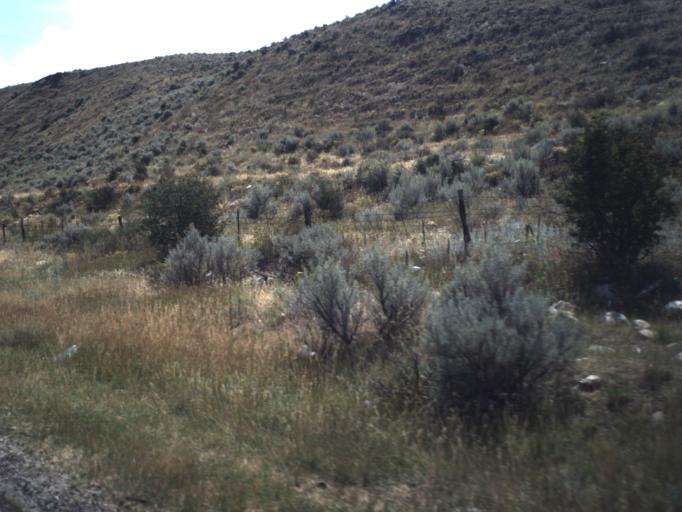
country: US
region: Utah
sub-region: Rich County
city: Randolph
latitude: 41.8510
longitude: -111.3588
